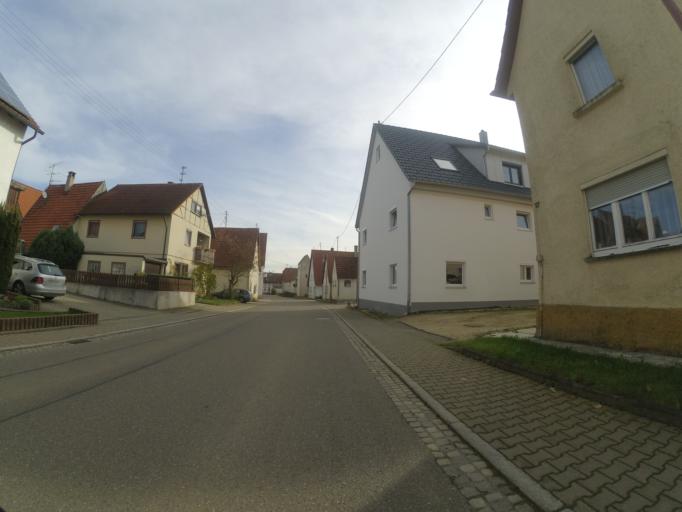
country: DE
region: Baden-Wuerttemberg
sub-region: Tuebingen Region
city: Blaubeuren
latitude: 48.4266
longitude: 9.8608
